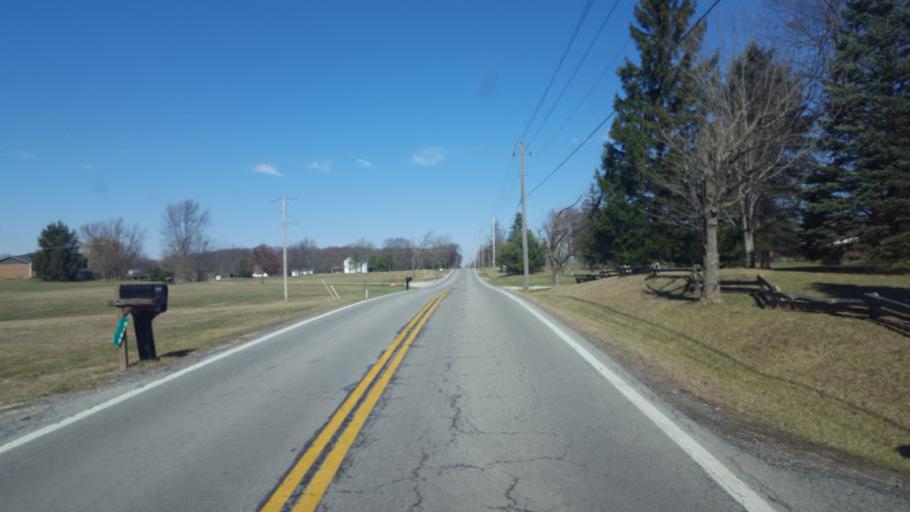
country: US
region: Ohio
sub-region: Marion County
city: Prospect
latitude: 40.5051
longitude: -83.1901
